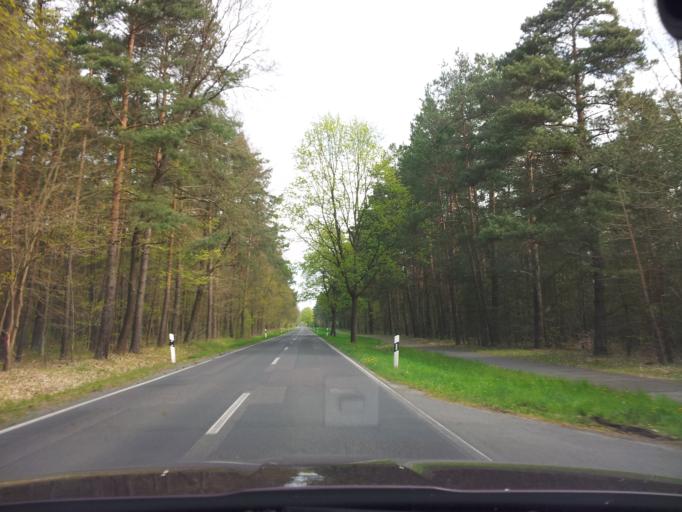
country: DE
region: Brandenburg
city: Rehfelde
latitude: 52.4730
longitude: 13.9084
